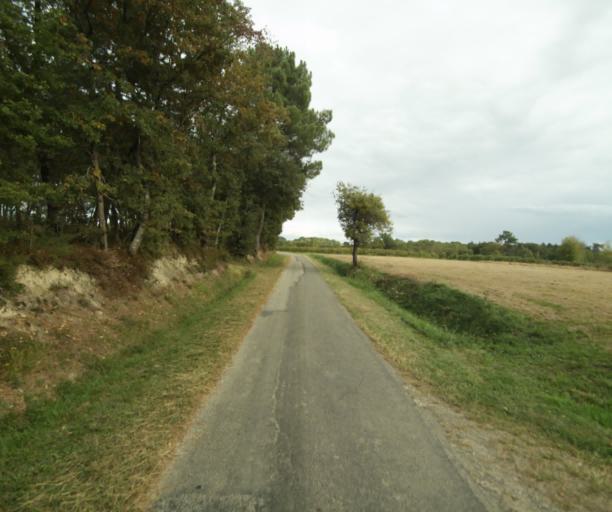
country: FR
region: Midi-Pyrenees
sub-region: Departement du Gers
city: Eauze
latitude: 43.9166
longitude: 0.1031
